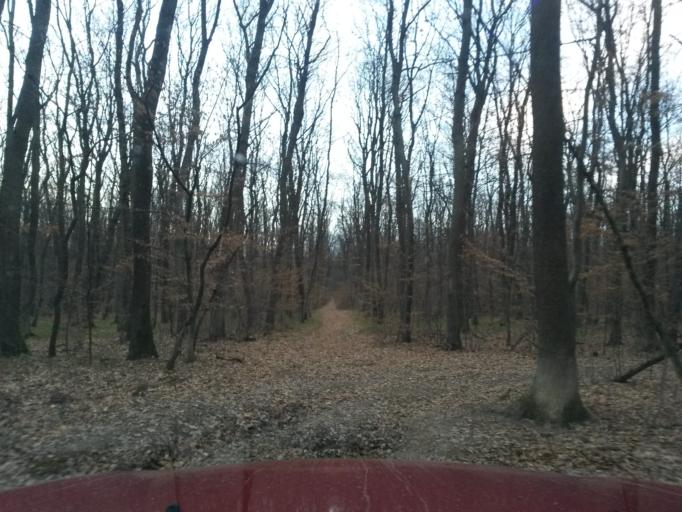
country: SK
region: Kosicky
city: Kosice
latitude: 48.6986
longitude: 21.3060
